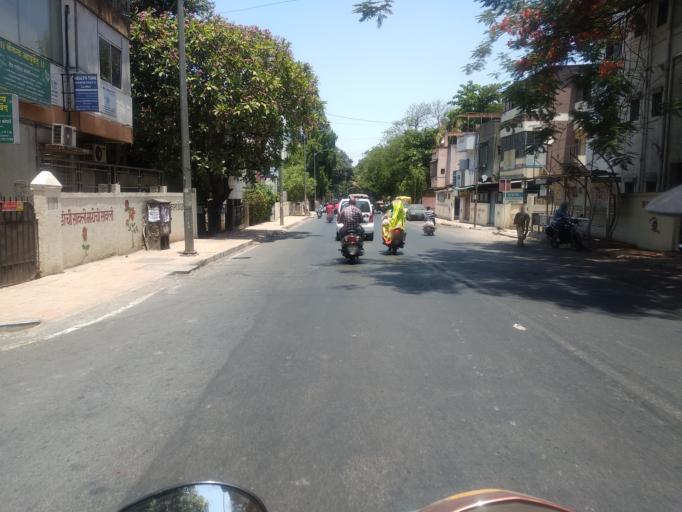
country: IN
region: Maharashtra
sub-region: Pune Division
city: Pune
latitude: 18.5049
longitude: 73.8432
